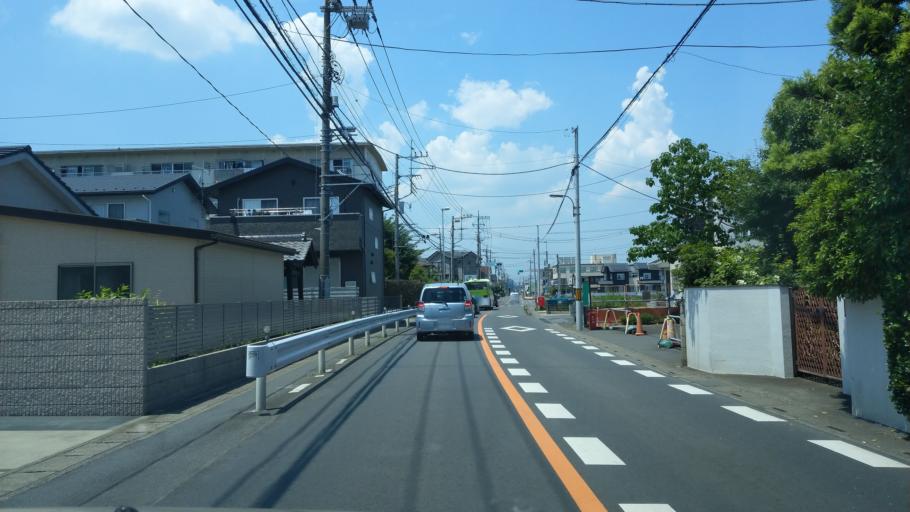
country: JP
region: Saitama
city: Saitama
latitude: 35.8656
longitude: 139.6822
